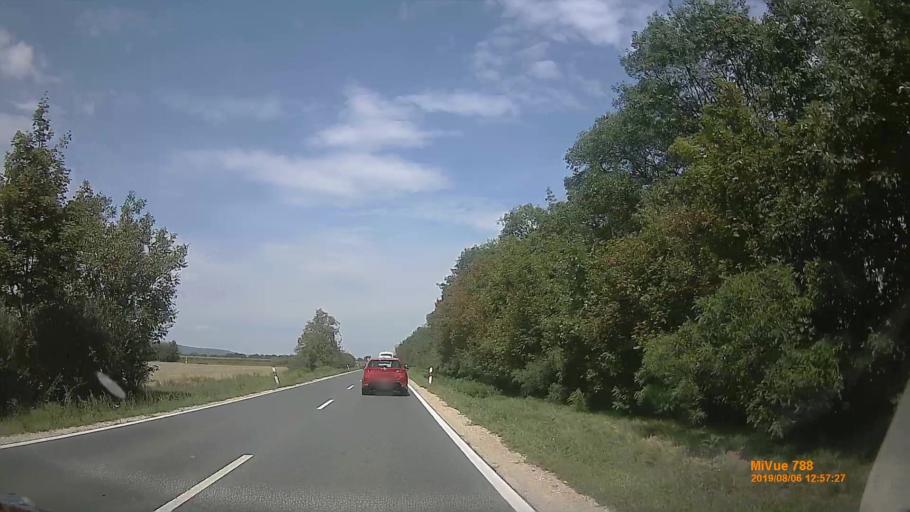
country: HU
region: Vas
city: Gencsapati
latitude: 47.2957
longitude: 16.6074
